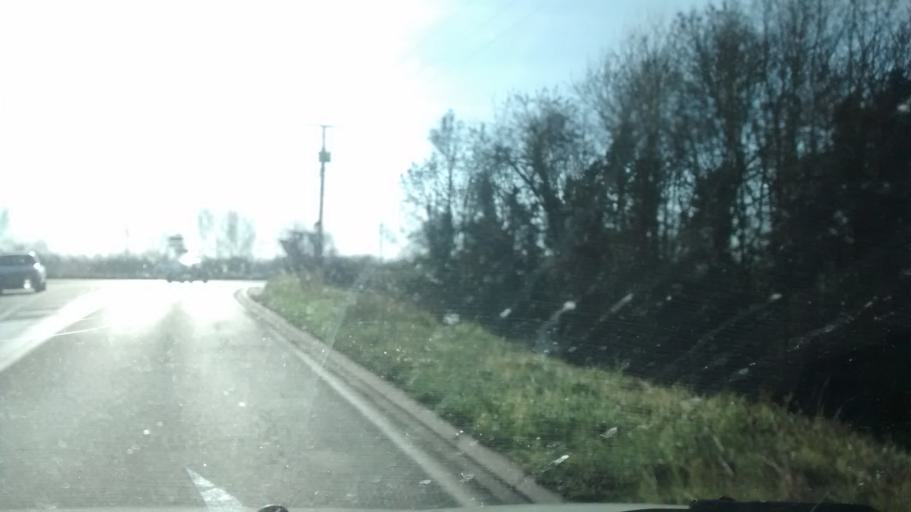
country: FR
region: Centre
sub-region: Departement d'Indre-et-Loire
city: Amboise
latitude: 47.4136
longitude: 0.9633
